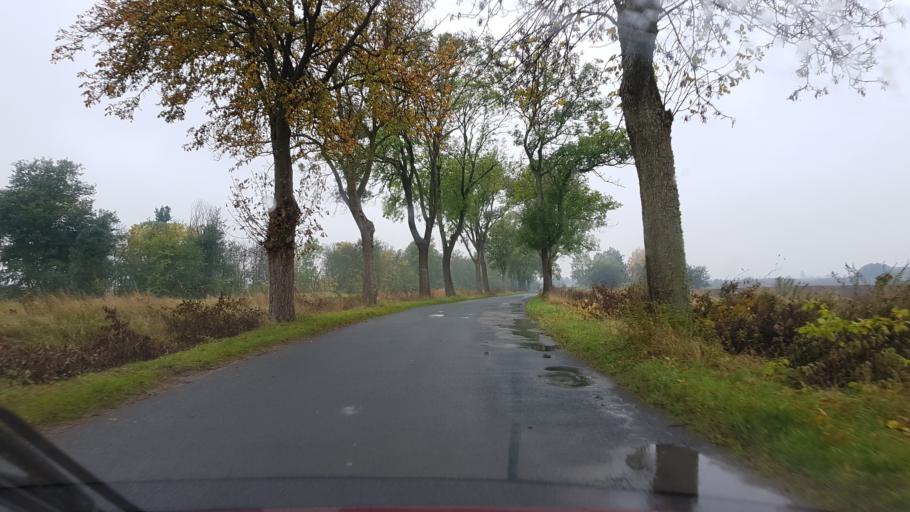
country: PL
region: Greater Poland Voivodeship
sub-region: Powiat zlotowski
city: Tarnowka
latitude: 53.3468
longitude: 16.8951
